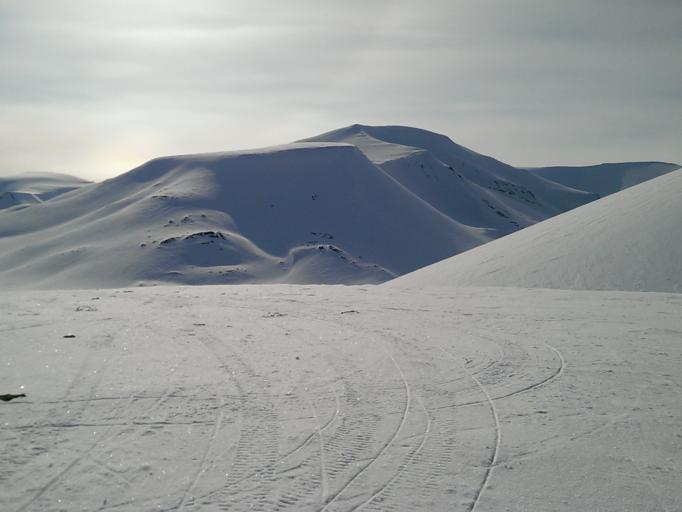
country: SJ
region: Svalbard
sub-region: Spitsbergen
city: Longyearbyen
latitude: 78.1060
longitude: 15.7769
